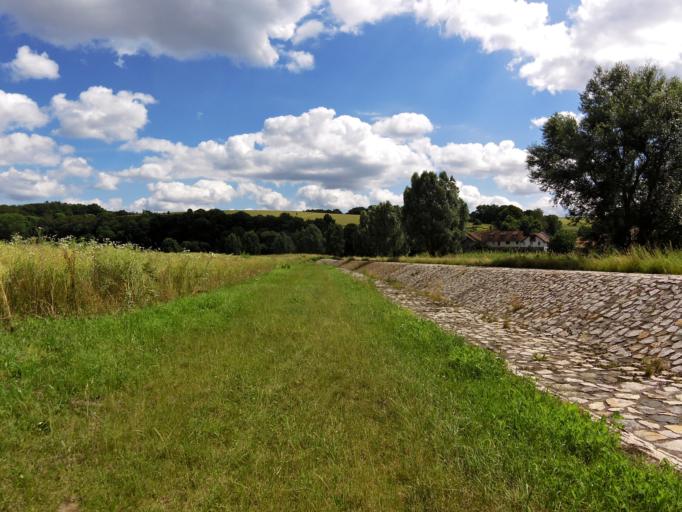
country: DE
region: Hesse
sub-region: Regierungsbezirk Kassel
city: Herleshausen
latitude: 50.9968
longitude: 10.1913
